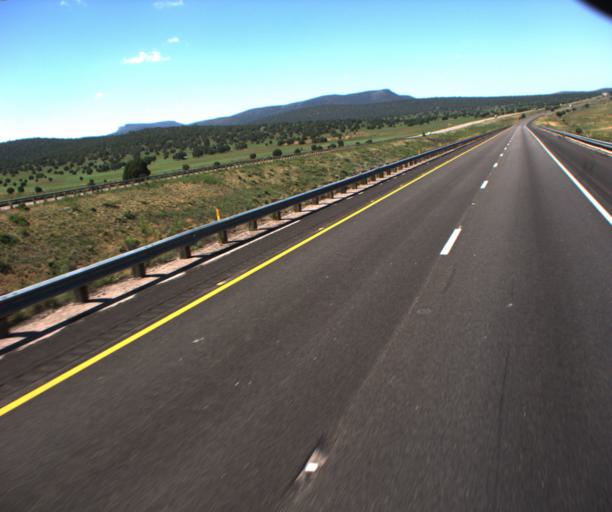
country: US
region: Arizona
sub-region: Mohave County
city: Peach Springs
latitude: 35.2379
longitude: -113.2057
